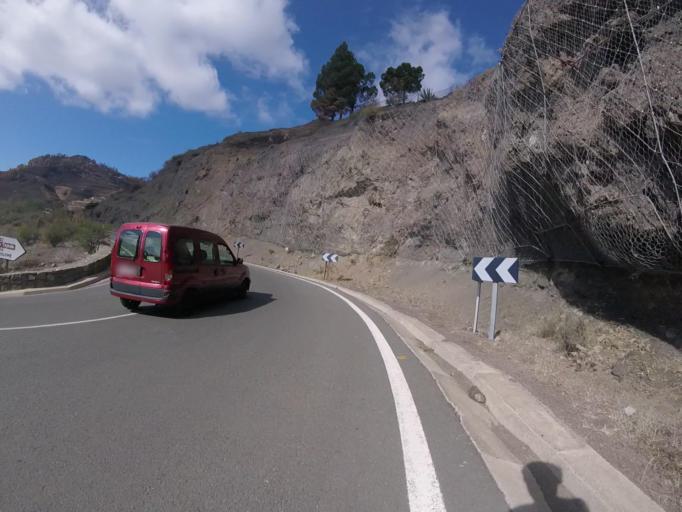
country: ES
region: Canary Islands
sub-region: Provincia de Las Palmas
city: Tejeda
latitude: 28.0094
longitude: -15.5899
